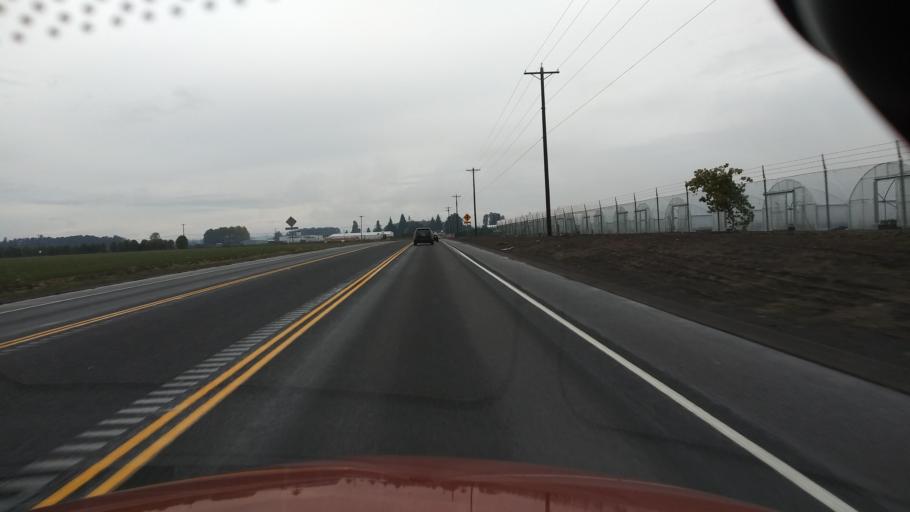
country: US
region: Oregon
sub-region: Washington County
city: Cornelius
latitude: 45.5646
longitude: -123.0528
